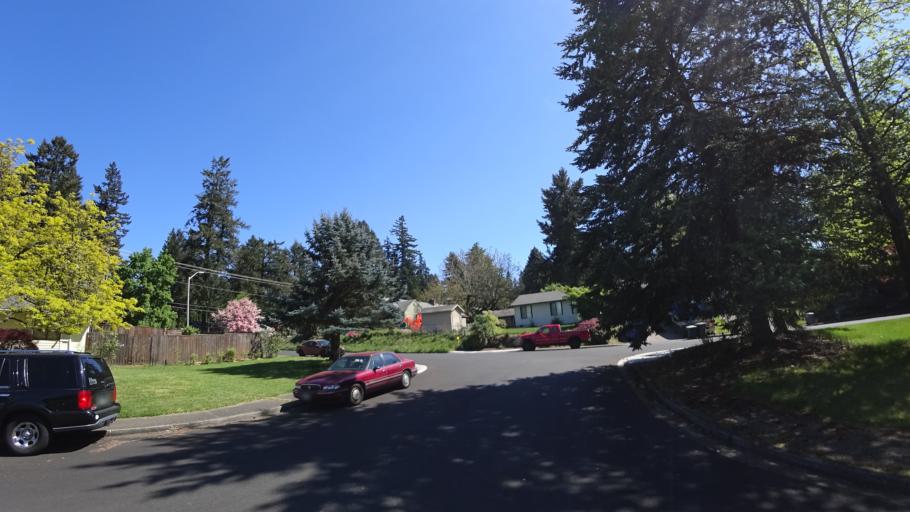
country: US
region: Oregon
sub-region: Washington County
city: Hillsboro
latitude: 45.5205
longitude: -122.9590
